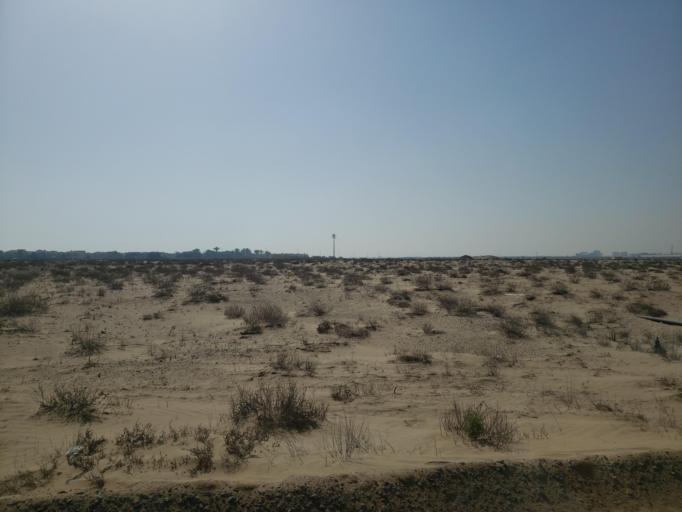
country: AE
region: Umm al Qaywayn
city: Umm al Qaywayn
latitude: 25.5265
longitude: 55.5889
